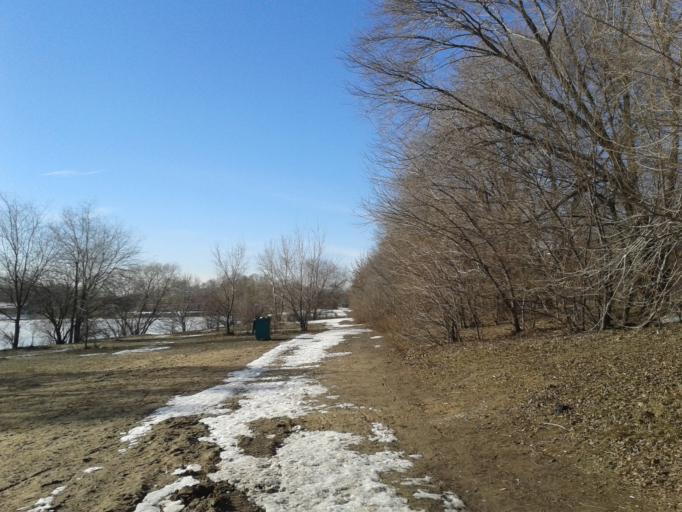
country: RU
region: Moscow
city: Strogino
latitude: 55.8001
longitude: 37.4161
